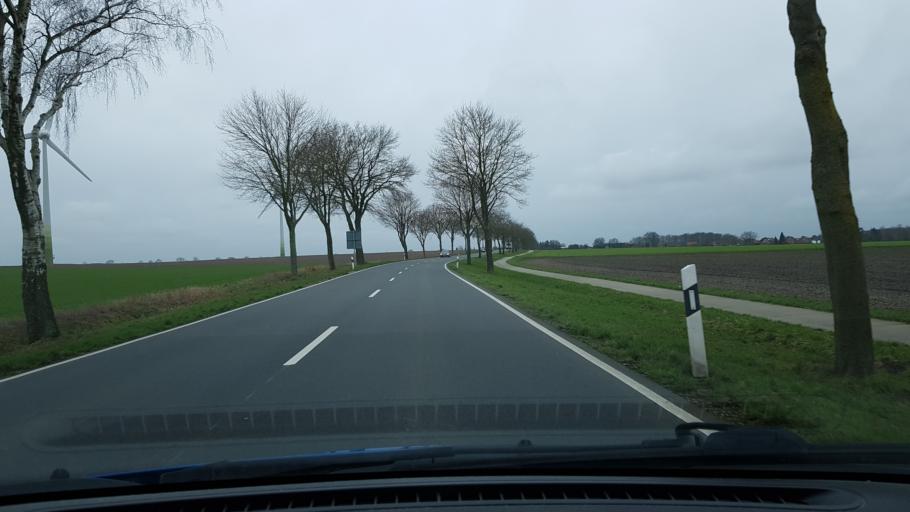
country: DE
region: Lower Saxony
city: Oetzen
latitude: 53.0092
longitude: 10.6940
